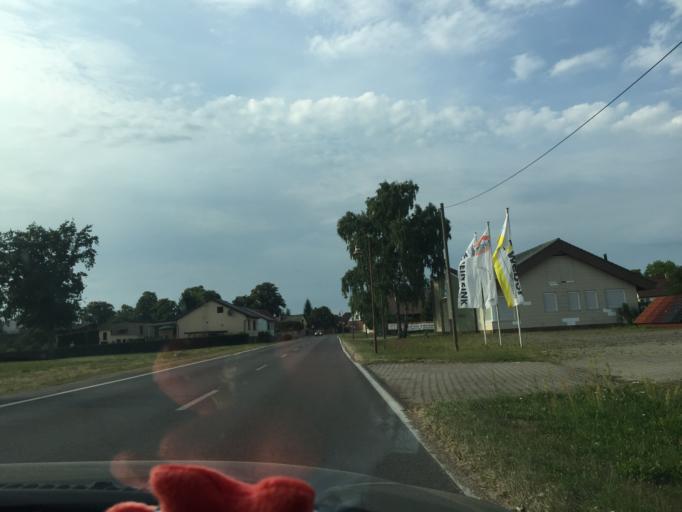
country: DE
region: Brandenburg
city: Zehdenick
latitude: 52.9429
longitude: 13.3870
